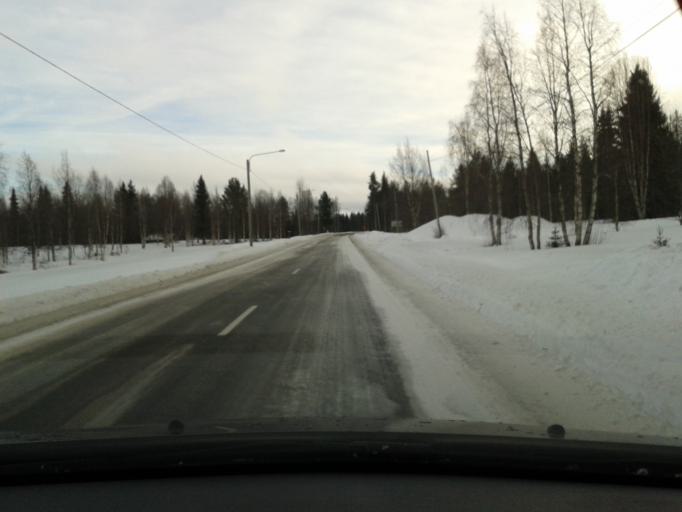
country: SE
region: Vaesterbotten
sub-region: Vilhelmina Kommun
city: Sjoberg
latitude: 64.6472
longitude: 16.3450
